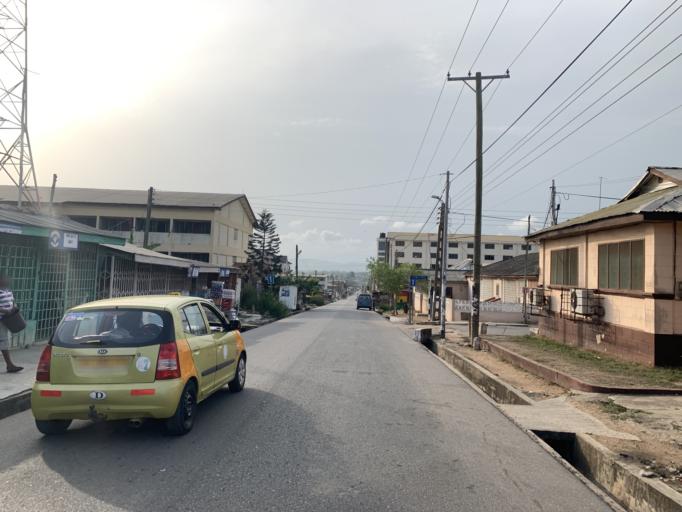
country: GH
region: Central
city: Winneba
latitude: 5.3441
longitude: -0.6249
